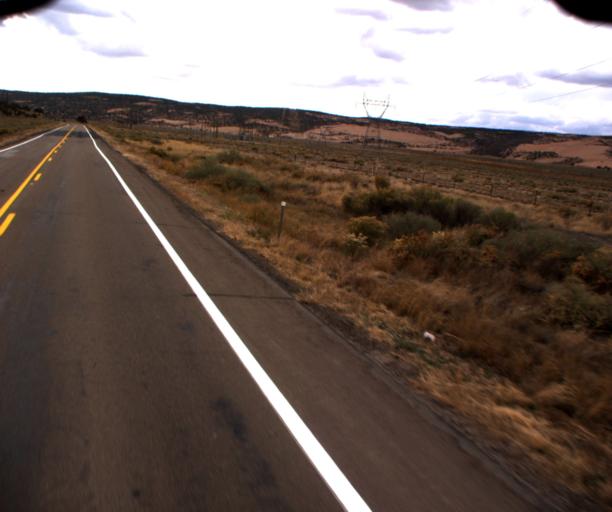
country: US
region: Arizona
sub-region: Navajo County
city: Kayenta
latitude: 36.6230
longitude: -110.4611
